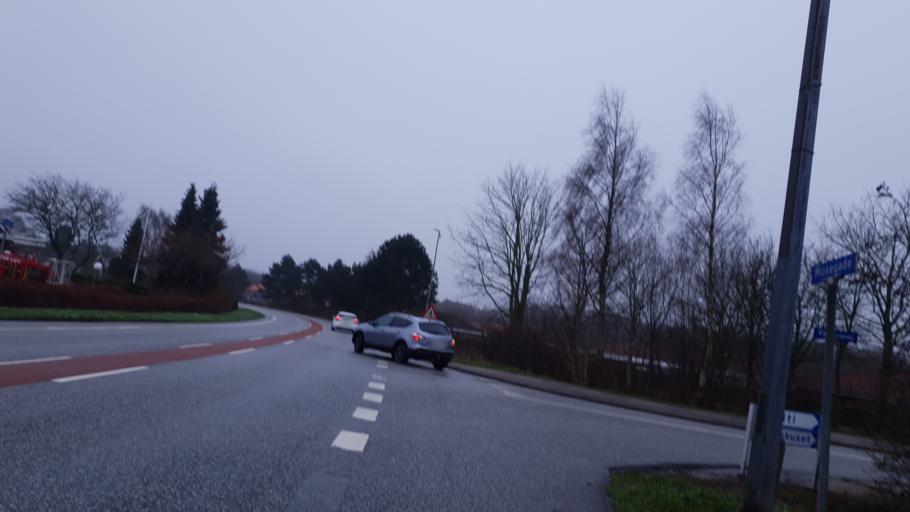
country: DK
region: Central Jutland
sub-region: Hedensted Kommune
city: Hedensted
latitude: 55.7775
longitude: 9.6959
